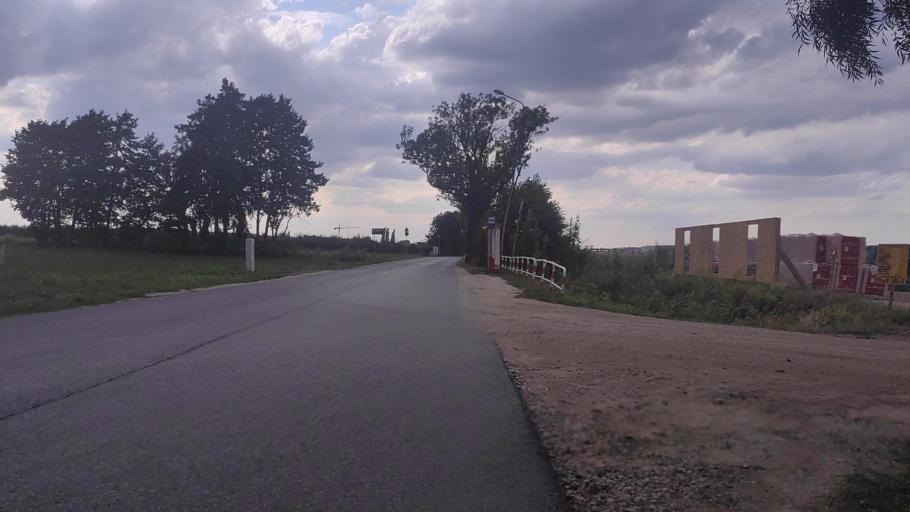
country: PL
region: Greater Poland Voivodeship
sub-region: Powiat poznanski
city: Swarzedz
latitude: 52.3872
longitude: 17.1062
